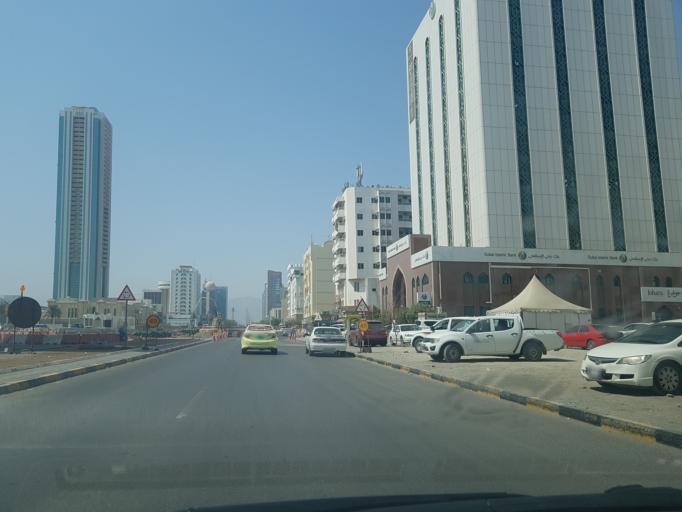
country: AE
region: Al Fujayrah
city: Al Fujayrah
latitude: 25.1221
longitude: 56.3379
